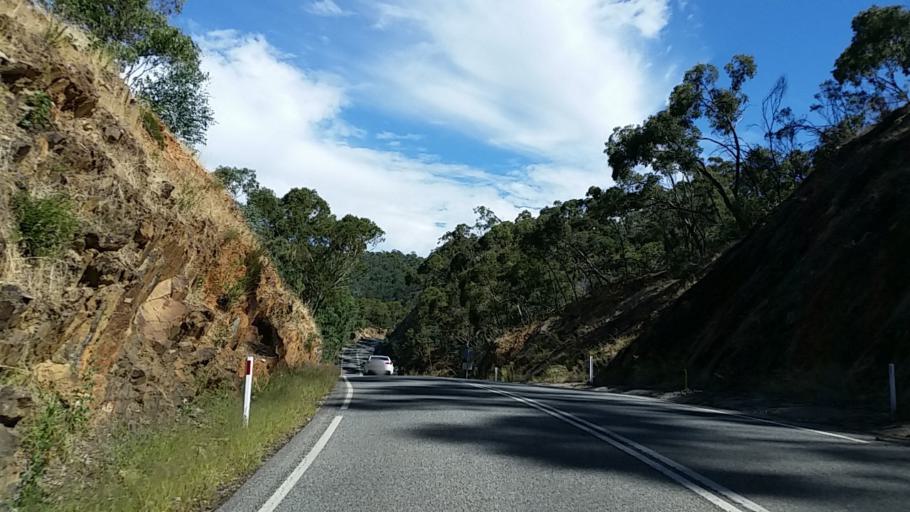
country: AU
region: South Australia
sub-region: Campbelltown
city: Athelstone
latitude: -34.8615
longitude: 138.7843
